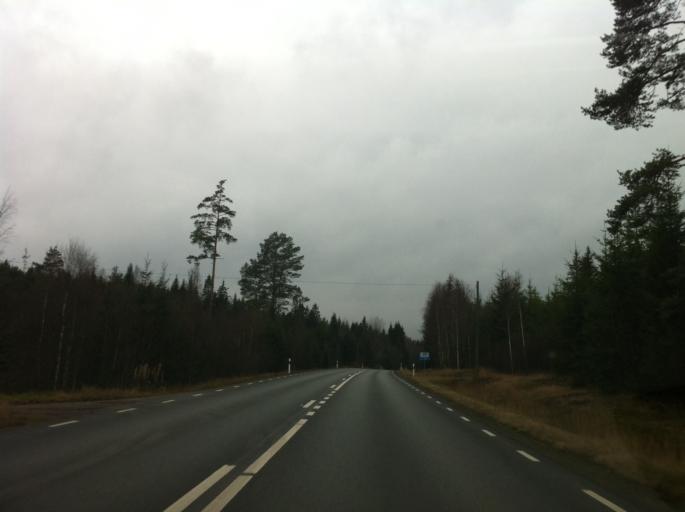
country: SE
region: Joenkoeping
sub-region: Savsjo Kommun
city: Saevsjoe
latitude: 57.3920
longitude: 14.7328
